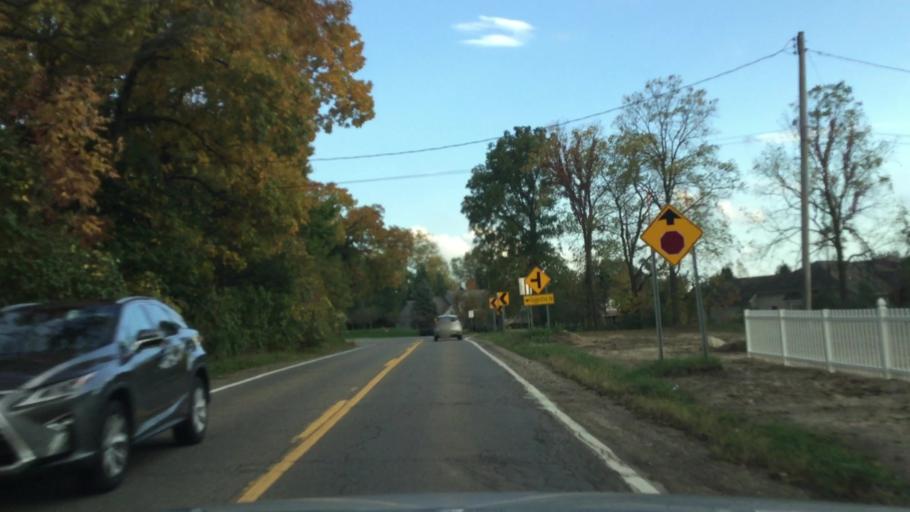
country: US
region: Michigan
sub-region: Oakland County
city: Wolverine Lake
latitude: 42.6428
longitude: -83.4963
